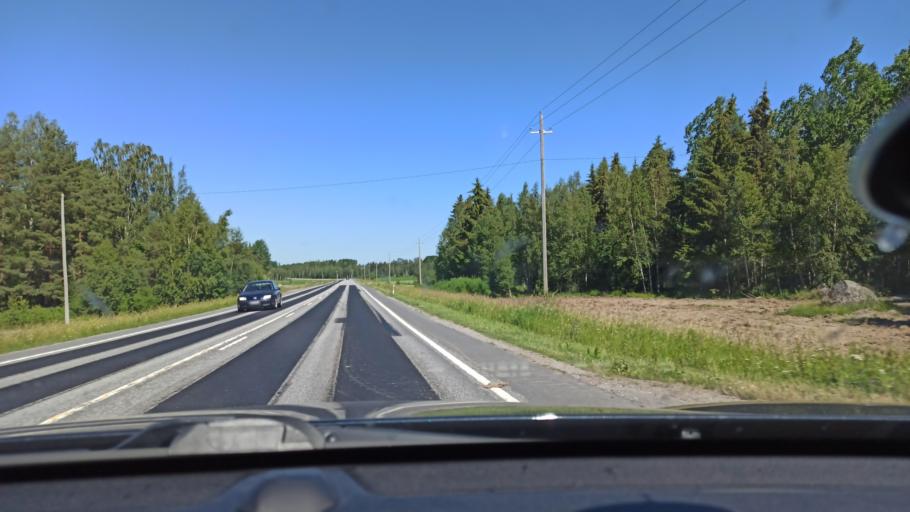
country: FI
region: Ostrobothnia
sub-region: Vaasa
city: Voera
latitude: 63.2177
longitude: 22.2139
